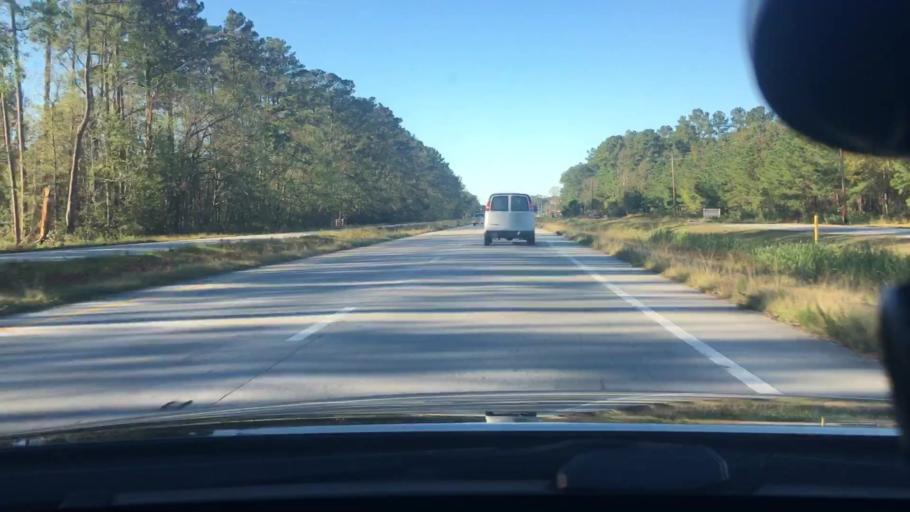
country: US
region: North Carolina
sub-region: Craven County
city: Fairfield Harbour
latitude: 35.0320
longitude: -77.0038
